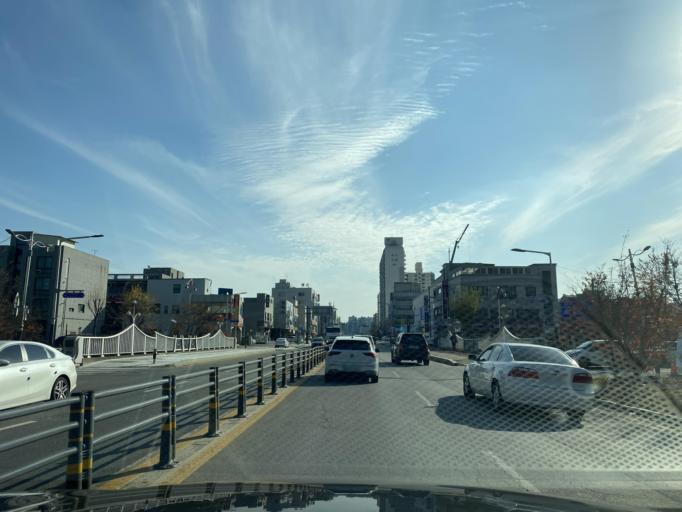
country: KR
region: Chungcheongnam-do
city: Cheonan
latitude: 36.8054
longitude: 127.1588
